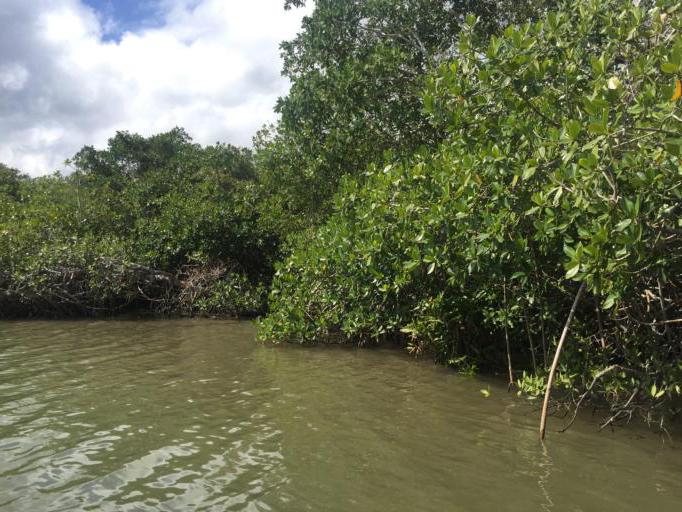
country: MX
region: Veracruz
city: Tecolutla
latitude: 20.4659
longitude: -97.0087
